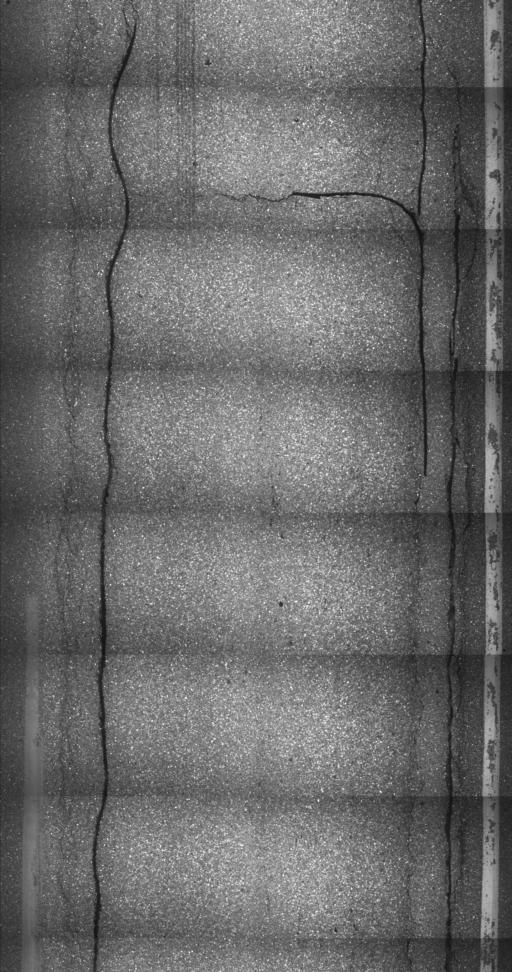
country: US
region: Vermont
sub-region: Franklin County
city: Saint Albans
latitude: 44.7480
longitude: -73.1129
